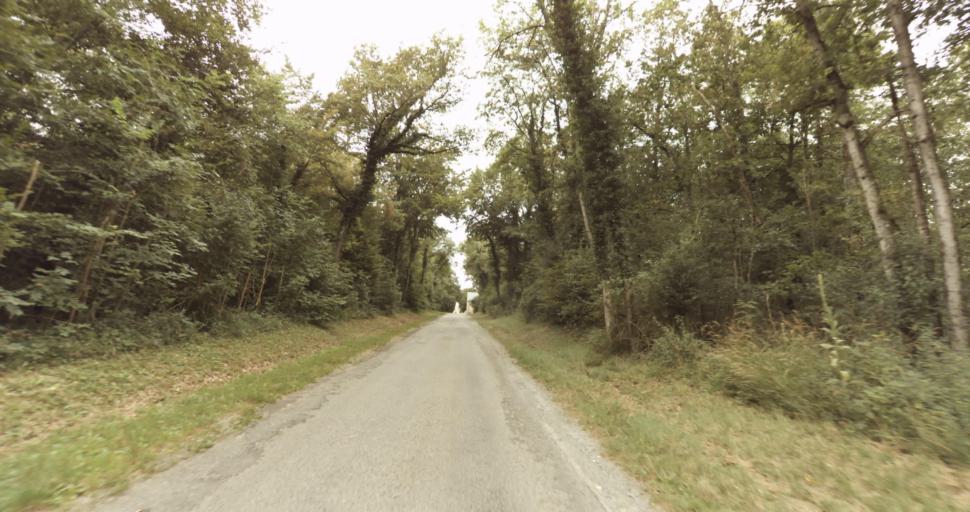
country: FR
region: Haute-Normandie
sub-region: Departement de l'Eure
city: Menilles
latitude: 49.0302
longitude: 1.3096
